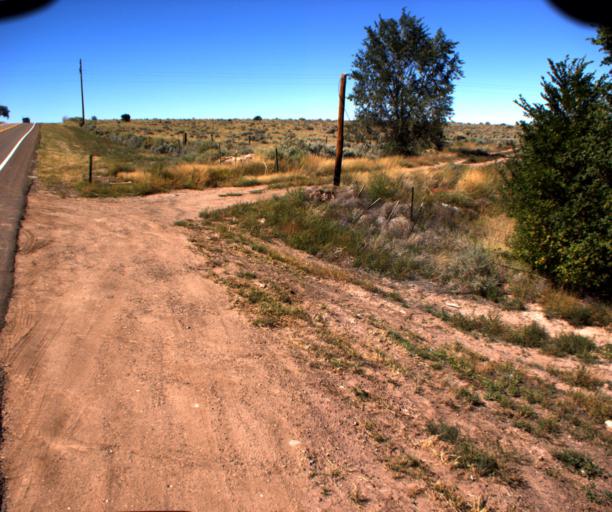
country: US
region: Arizona
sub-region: Apache County
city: Saint Johns
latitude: 34.5061
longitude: -109.4088
